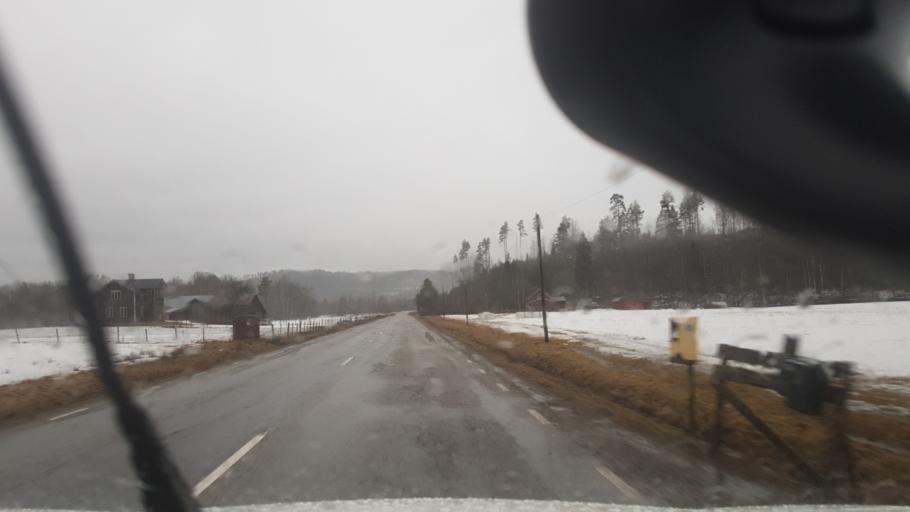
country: SE
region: Vaermland
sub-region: Arjangs Kommun
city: Arjaeng
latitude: 59.5782
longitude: 12.1234
